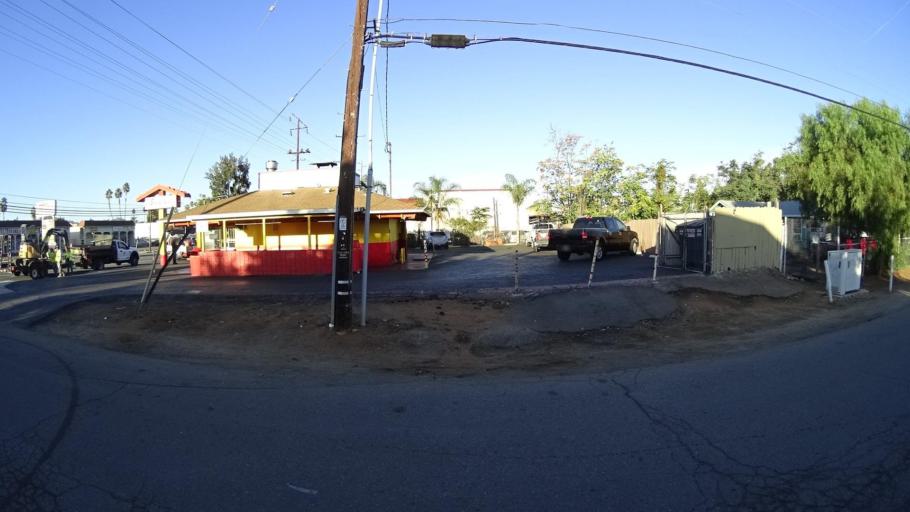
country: US
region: California
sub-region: San Diego County
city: Bostonia
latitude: 32.8081
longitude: -116.9481
